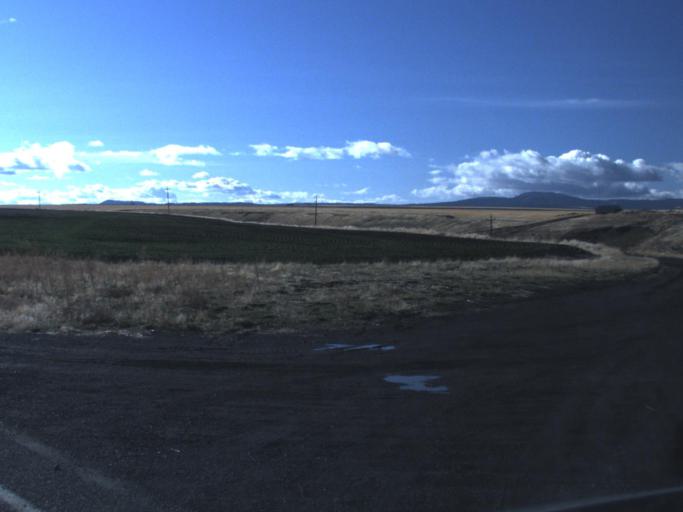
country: US
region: Washington
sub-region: Asotin County
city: Asotin
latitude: 46.2220
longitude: -117.0703
